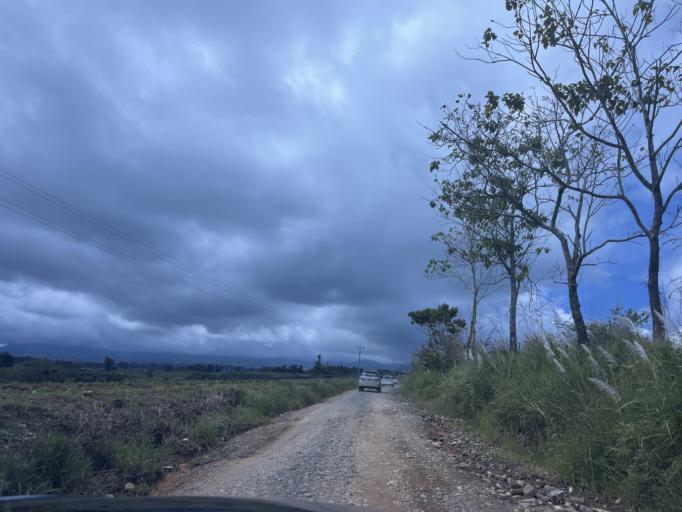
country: PH
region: Northern Mindanao
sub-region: Province of Bukidnon
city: Dalwangan
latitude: 8.2194
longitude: 124.9938
